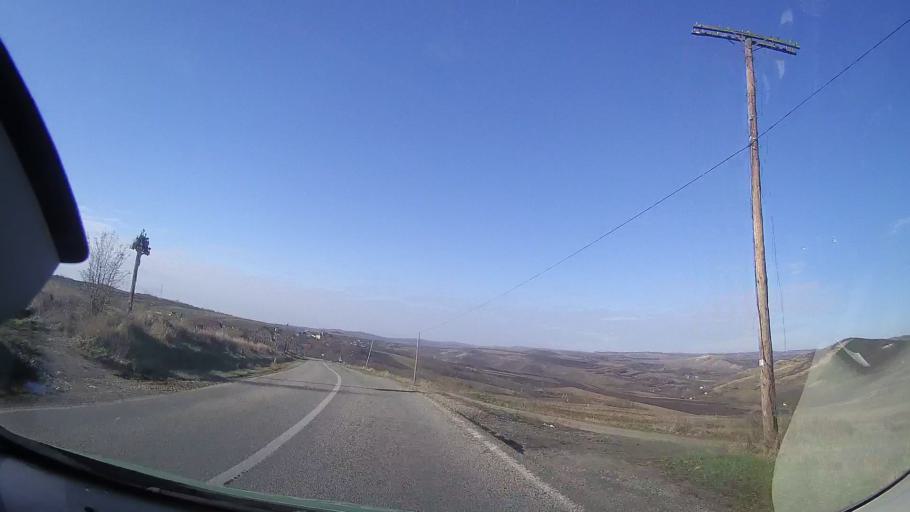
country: RO
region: Cluj
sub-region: Comuna Mociu
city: Mociu
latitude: 46.7893
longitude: 24.0817
